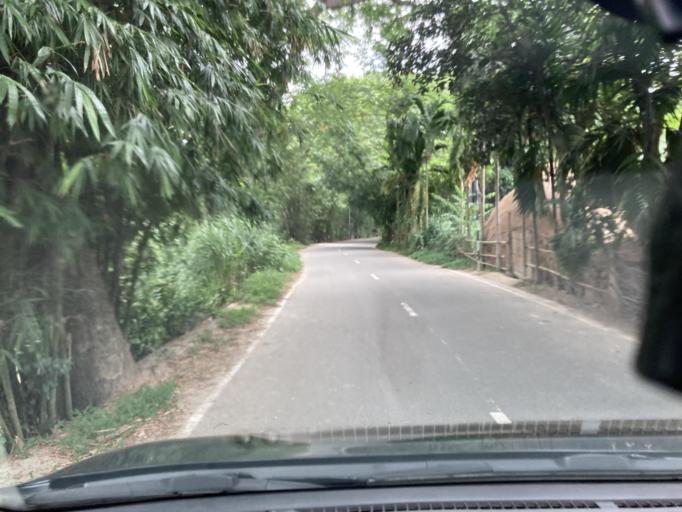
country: BD
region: Dhaka
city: Dohar
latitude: 23.7776
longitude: 90.0665
